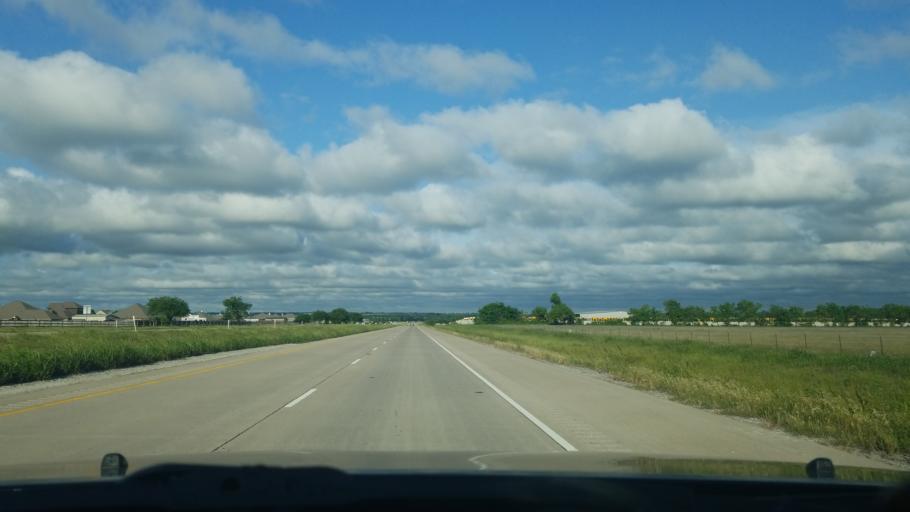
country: US
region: Texas
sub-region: Wise County
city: New Fairview
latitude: 33.2495
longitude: -97.4278
